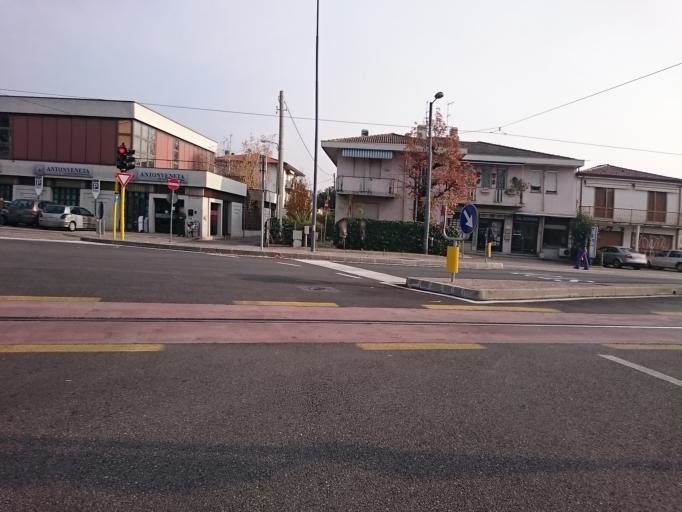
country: IT
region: Veneto
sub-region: Provincia di Padova
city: Mandriola-Sant'Agostino
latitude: 45.3809
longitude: 11.8691
